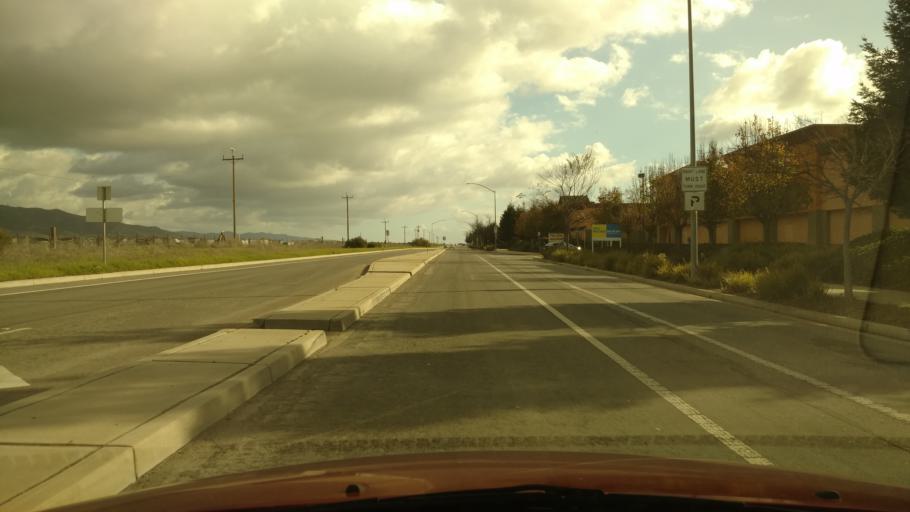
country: US
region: California
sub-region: Monterey County
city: Salinas
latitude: 36.6944
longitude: -121.5953
